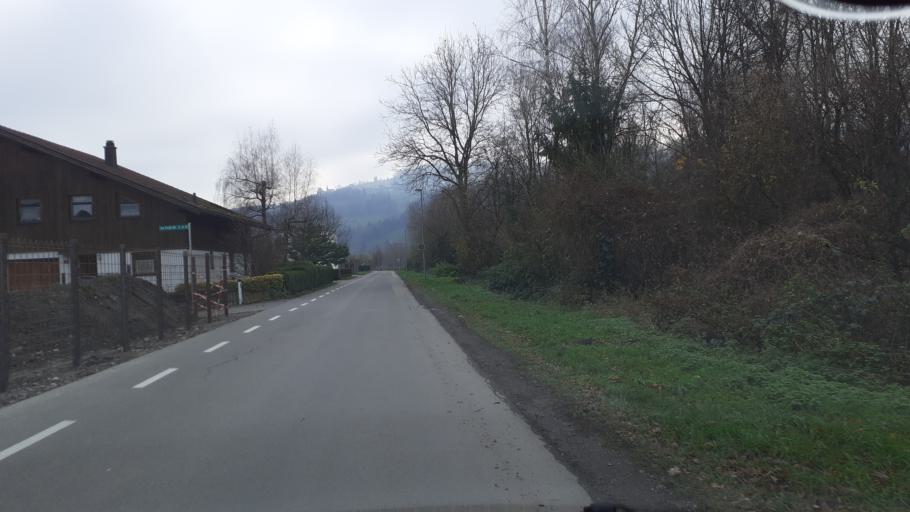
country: CH
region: Saint Gallen
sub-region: Wahlkreis Rheintal
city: Rheineck
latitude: 47.4723
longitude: 9.5899
